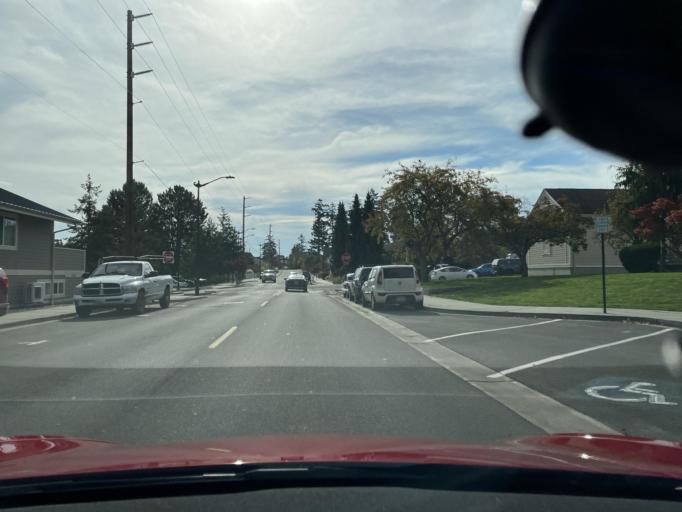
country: US
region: Washington
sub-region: San Juan County
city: Friday Harbor
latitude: 48.5350
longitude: -123.0204
